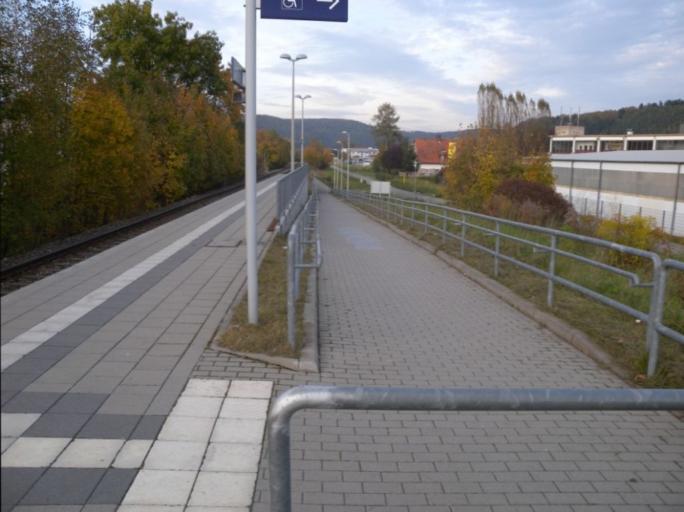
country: DE
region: Baden-Wuerttemberg
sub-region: Freiburg Region
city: Tuttlingen
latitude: 47.9930
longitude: 8.8239
